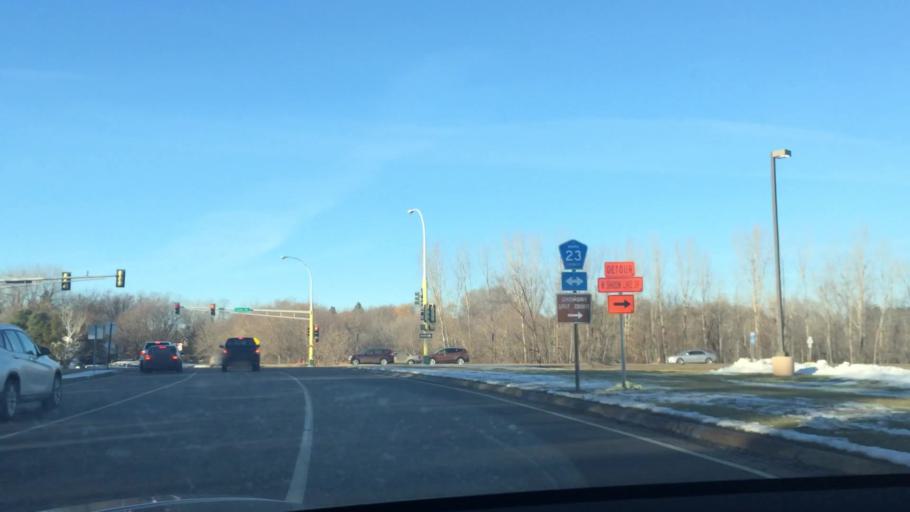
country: US
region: Minnesota
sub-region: Anoka County
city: Circle Pines
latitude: 45.1525
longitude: -93.1361
